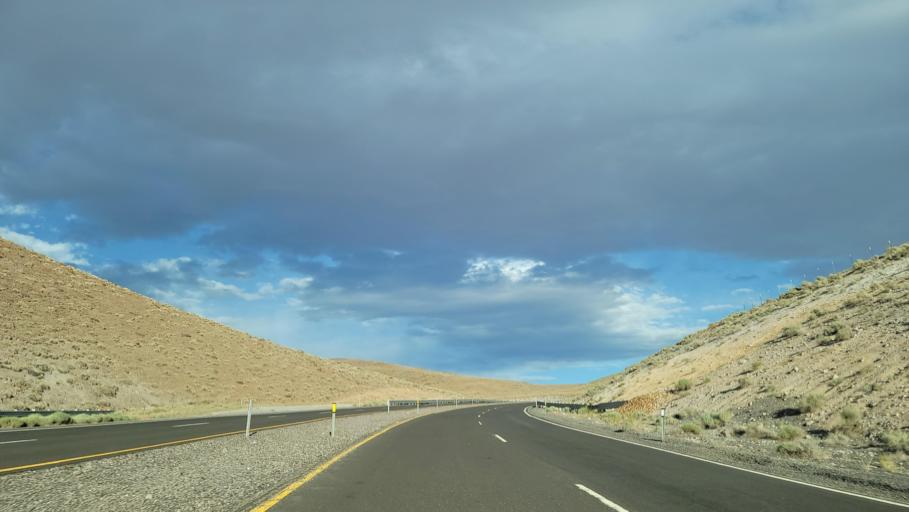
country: US
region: Nevada
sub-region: Lyon County
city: Stagecoach
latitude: 39.5117
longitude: -119.4666
